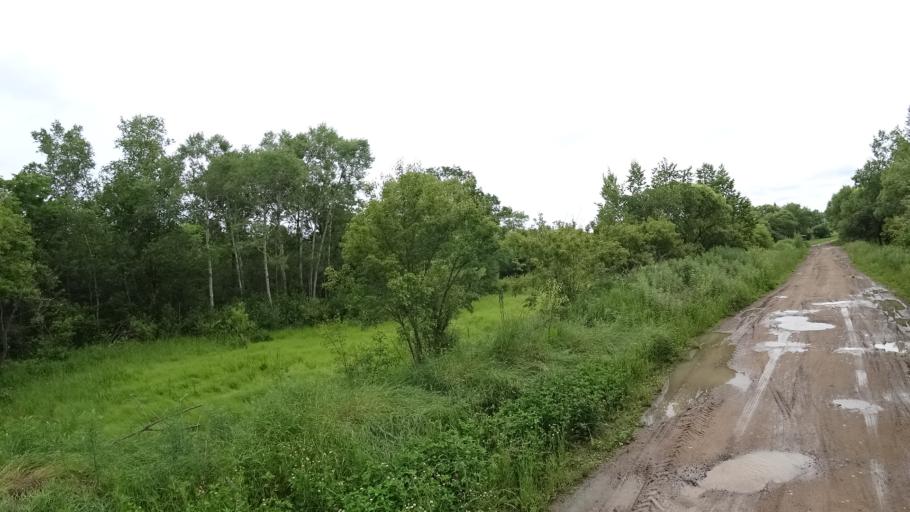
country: RU
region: Primorskiy
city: Novosysoyevka
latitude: 44.2550
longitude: 133.3726
